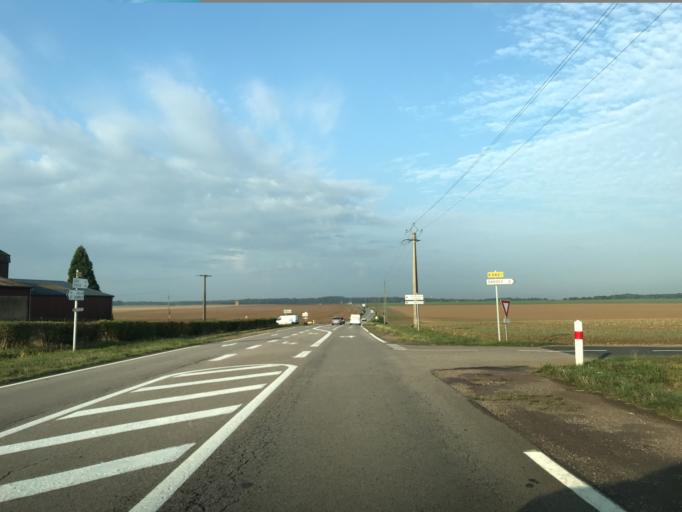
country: FR
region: Haute-Normandie
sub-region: Departement de l'Eure
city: Gravigny
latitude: 49.0725
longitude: 1.2235
